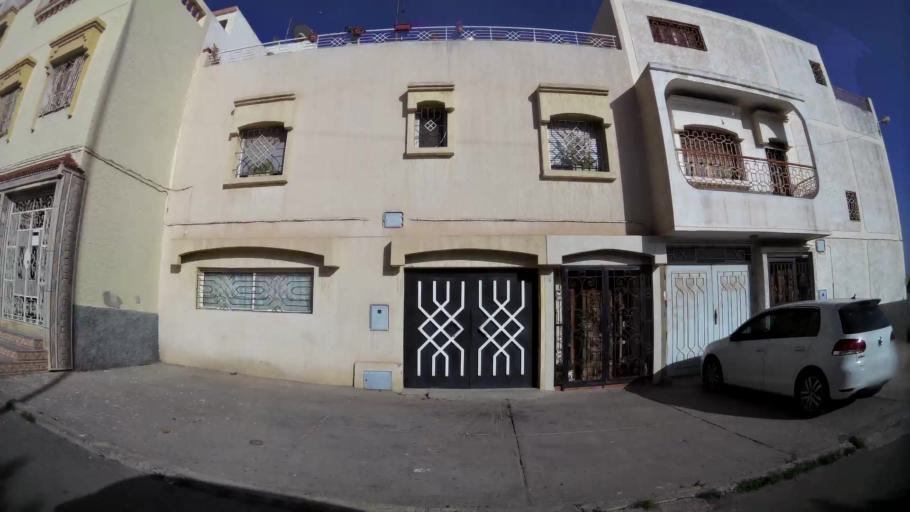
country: MA
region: Souss-Massa-Draa
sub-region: Agadir-Ida-ou-Tnan
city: Agadir
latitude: 30.4289
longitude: -9.5840
